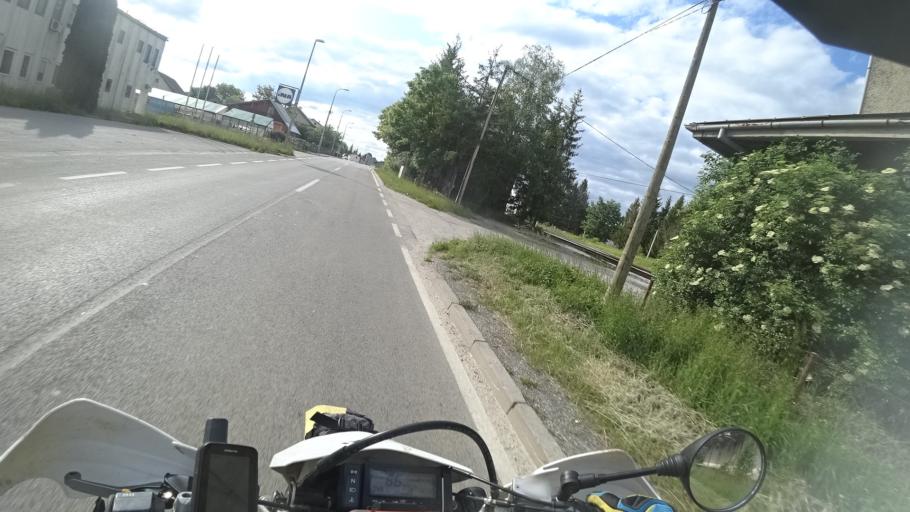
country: HR
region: Licko-Senjska
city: Gospic
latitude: 44.5337
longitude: 15.3973
